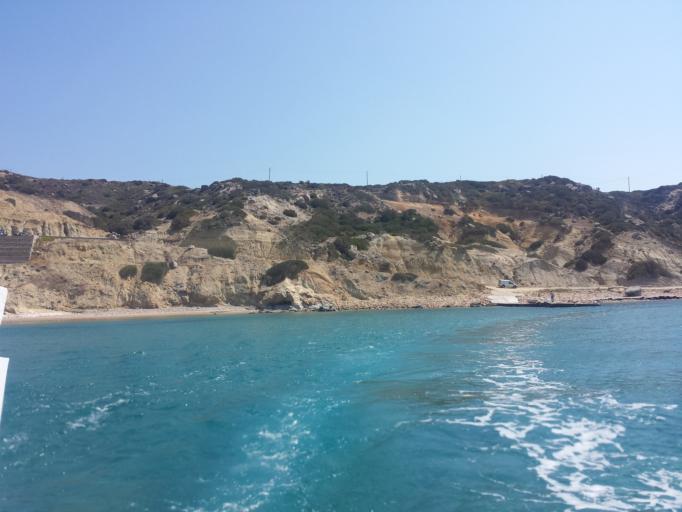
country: GR
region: South Aegean
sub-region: Nomos Kykladon
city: Adamas
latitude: 36.6619
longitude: 24.4286
